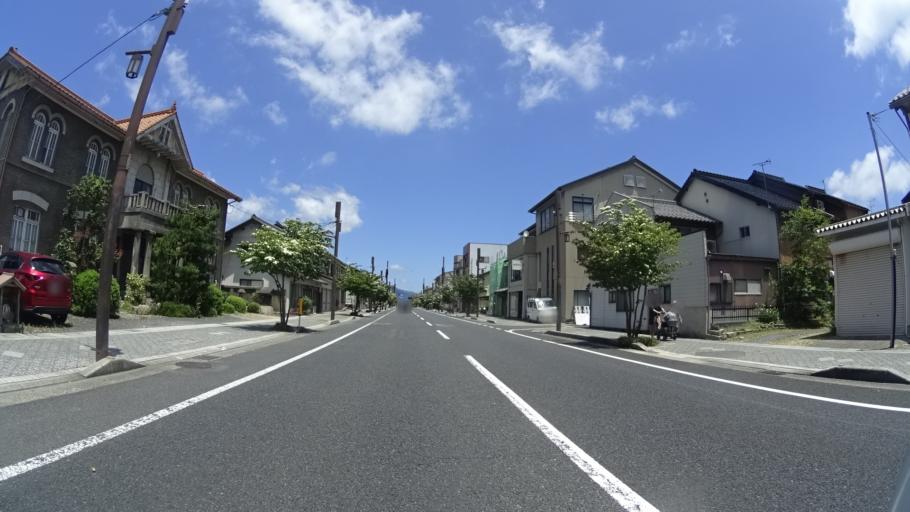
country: JP
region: Kyoto
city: Miyazu
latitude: 35.5337
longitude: 135.1932
